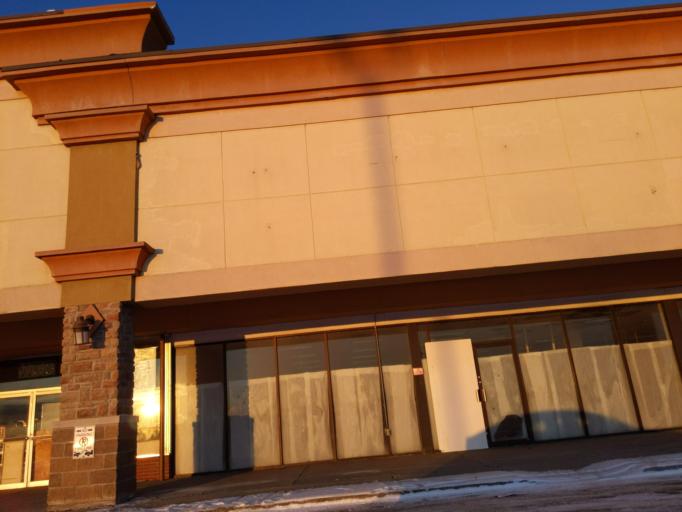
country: US
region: Michigan
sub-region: Ingham County
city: Lansing
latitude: 42.6984
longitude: -84.5712
